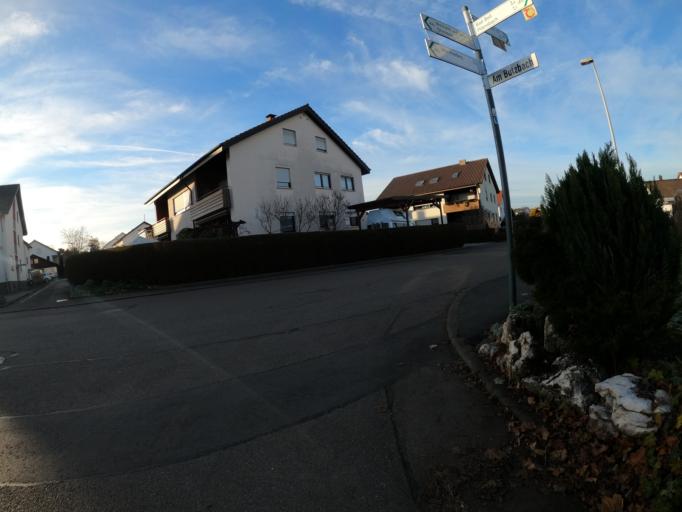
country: DE
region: Baden-Wuerttemberg
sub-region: Regierungsbezirk Stuttgart
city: Hattenhofen
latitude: 48.6648
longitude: 9.5765
